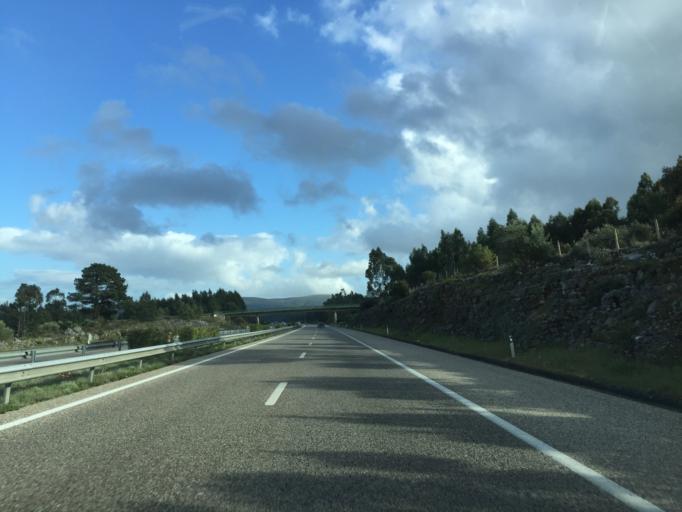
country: PT
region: Santarem
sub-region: Ourem
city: Fatima
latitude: 39.5982
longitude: -8.6699
